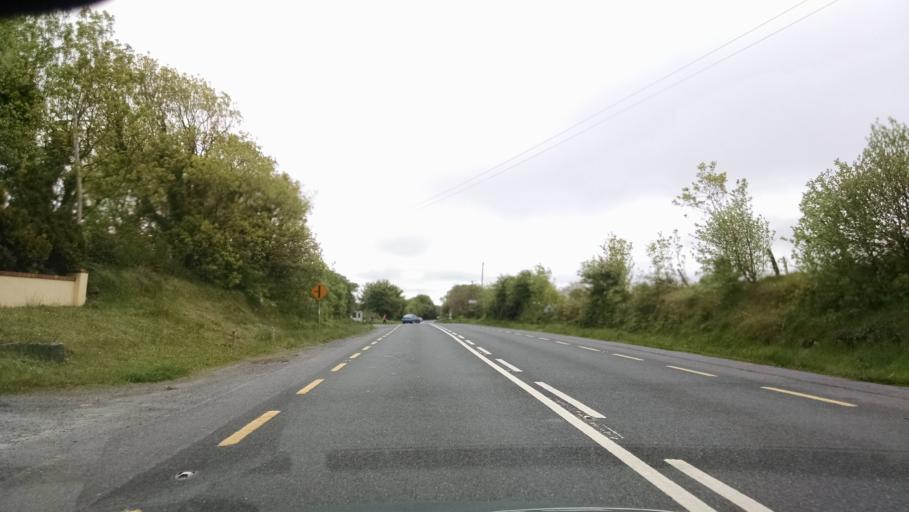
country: IE
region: Connaught
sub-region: County Galway
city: Claregalway
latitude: 53.4168
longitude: -9.0268
